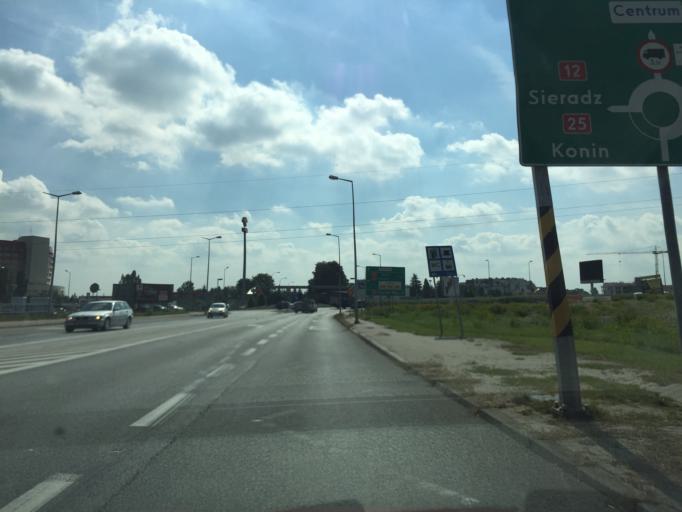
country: PL
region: Greater Poland Voivodeship
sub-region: Kalisz
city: Kalisz
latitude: 51.7645
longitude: 18.0605
